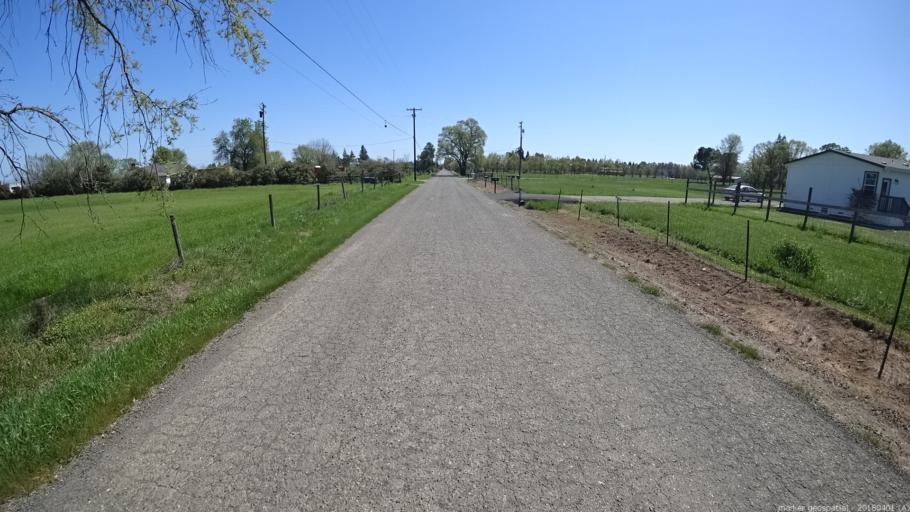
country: US
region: California
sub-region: Sacramento County
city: Rancho Murieta
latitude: 38.4561
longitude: -121.1802
